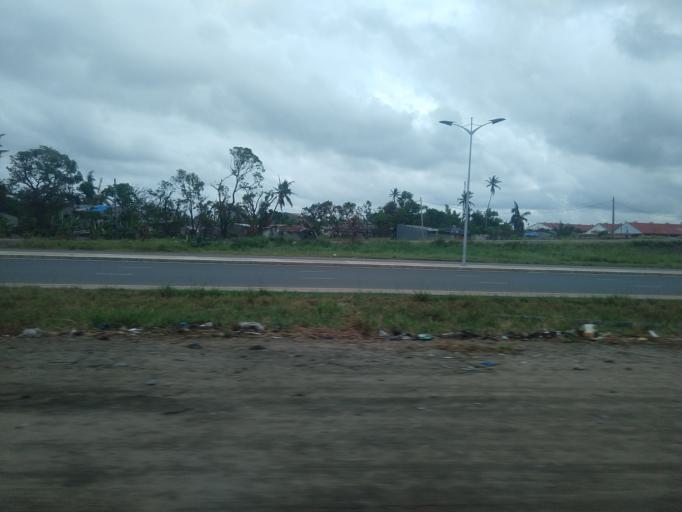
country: MZ
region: Sofala
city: Beira
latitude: -19.7838
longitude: 34.8779
